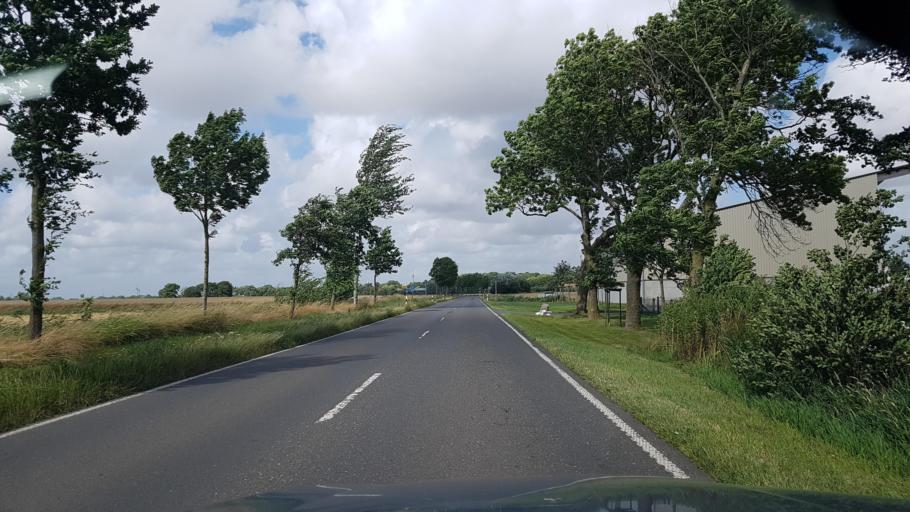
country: DE
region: Schleswig-Holstein
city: Suderdeich
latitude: 54.1940
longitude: 8.9026
